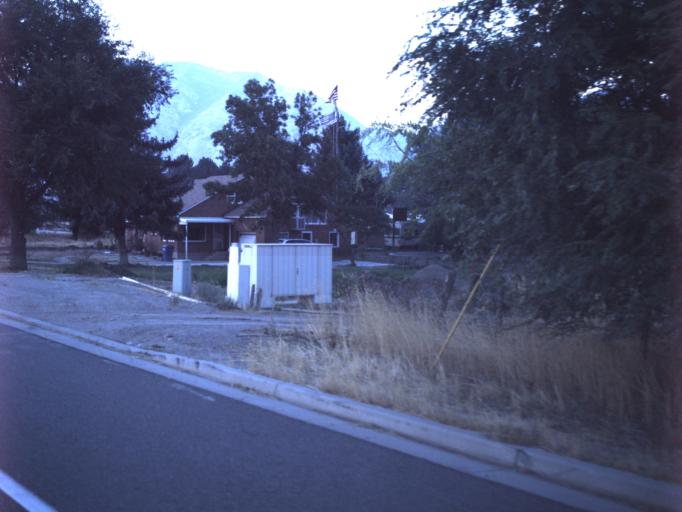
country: US
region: Utah
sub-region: Utah County
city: Mapleton
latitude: 40.1361
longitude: -111.5979
